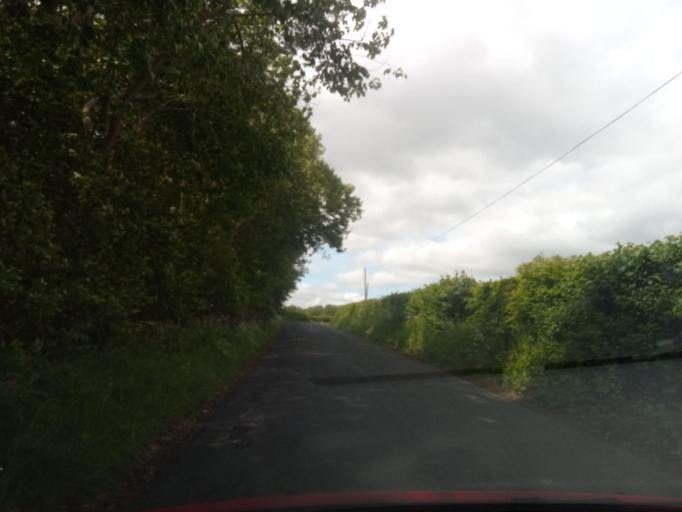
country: GB
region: Scotland
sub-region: The Scottish Borders
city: Galashiels
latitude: 55.5812
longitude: -2.8146
